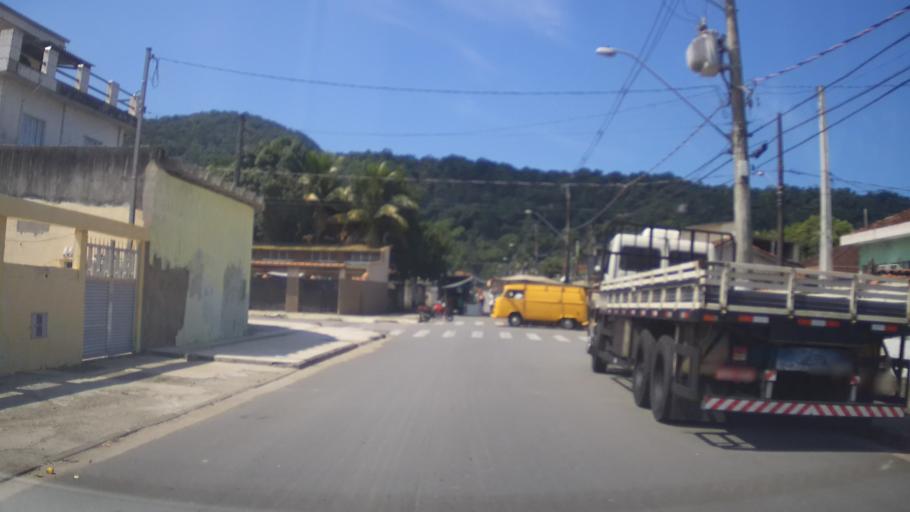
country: BR
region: Sao Paulo
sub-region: Praia Grande
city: Praia Grande
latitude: -23.9871
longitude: -46.3953
